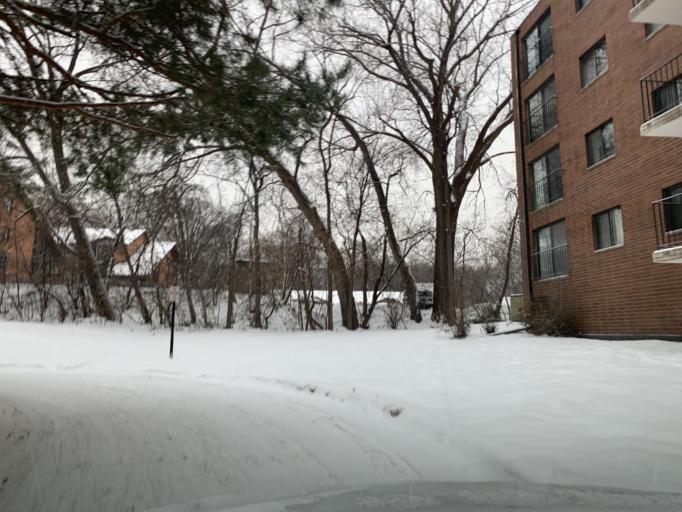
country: US
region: Minnesota
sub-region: Hennepin County
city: Saint Louis Park
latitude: 44.9498
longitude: -93.3352
